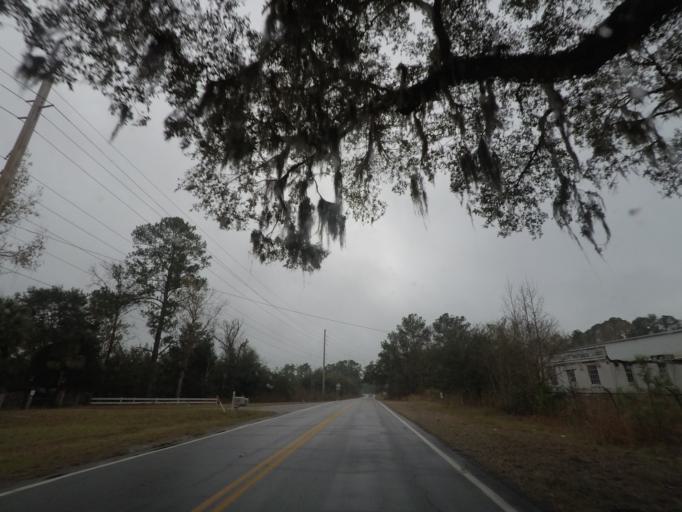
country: US
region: South Carolina
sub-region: Charleston County
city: Meggett
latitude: 32.6868
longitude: -80.3506
